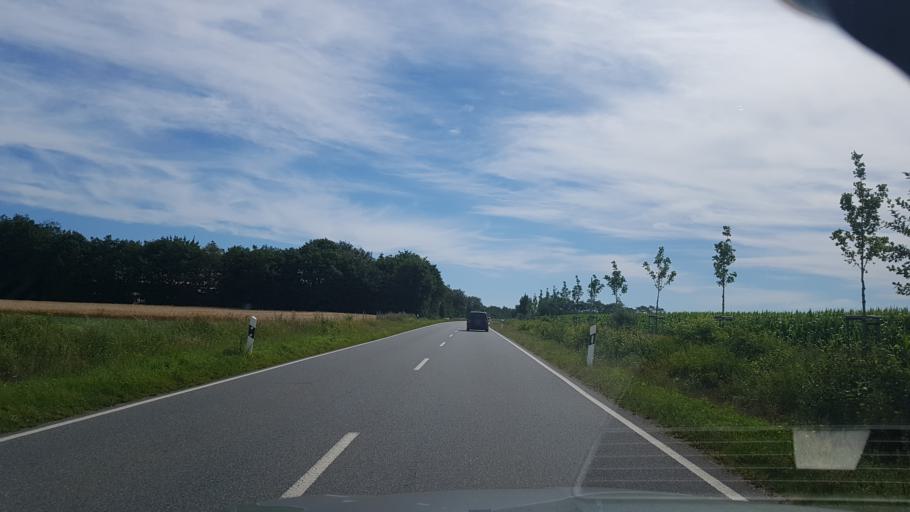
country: DE
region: Schleswig-Holstein
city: Osterby
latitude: 54.8018
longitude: 9.2608
